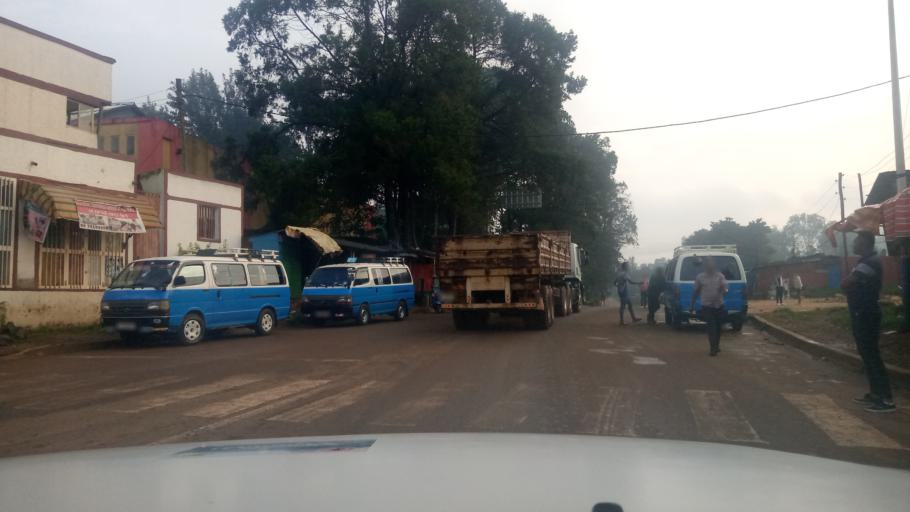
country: ET
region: Oromiya
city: Jima
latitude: 7.6766
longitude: 36.8344
